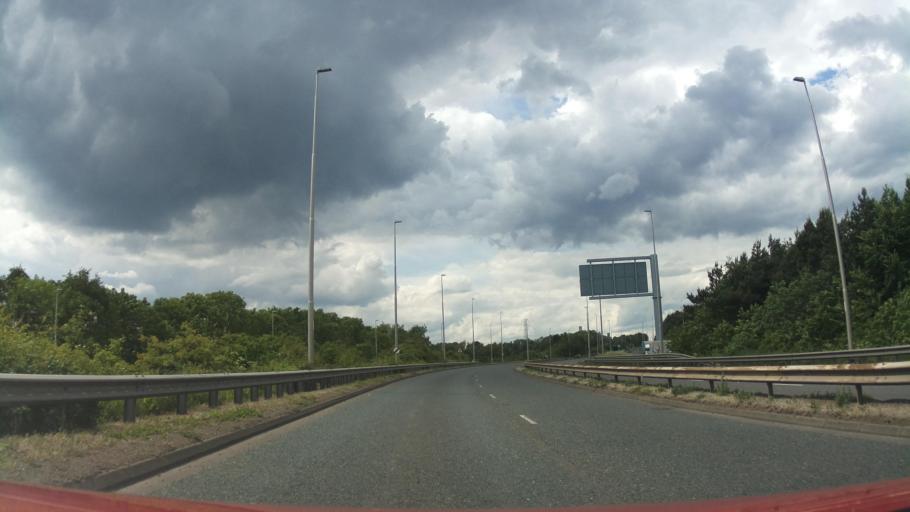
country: GB
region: England
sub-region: Sunderland
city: Washington
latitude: 54.9014
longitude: -1.5486
